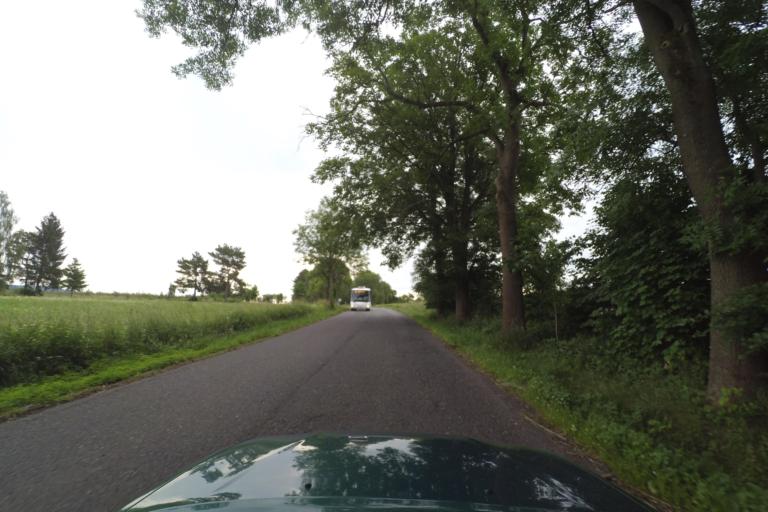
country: CZ
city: Cesky Dub
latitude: 50.6697
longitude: 15.0248
